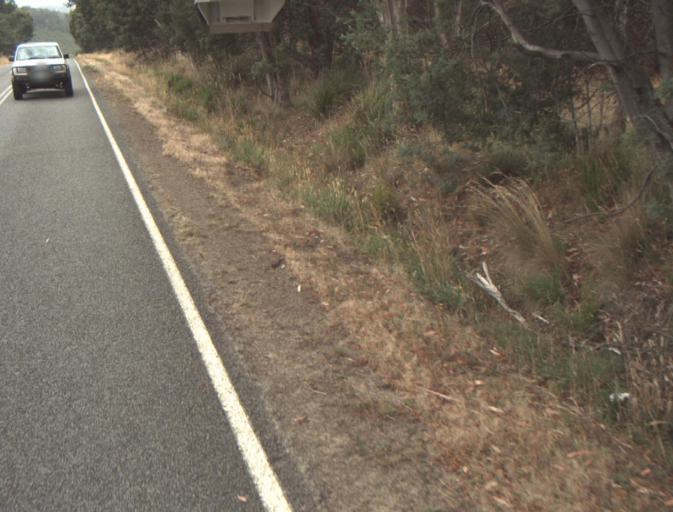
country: AU
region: Tasmania
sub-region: Northern Midlands
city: Evandale
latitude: -41.4738
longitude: 147.5431
